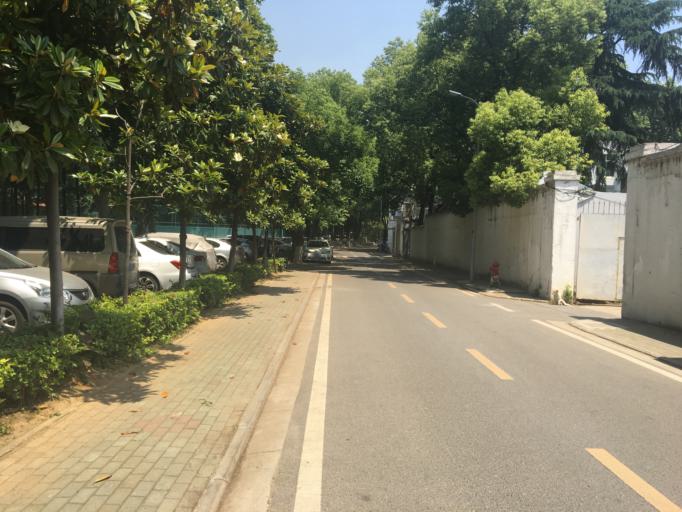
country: CN
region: Hubei
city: Guanshan
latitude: 30.5296
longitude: 114.3574
